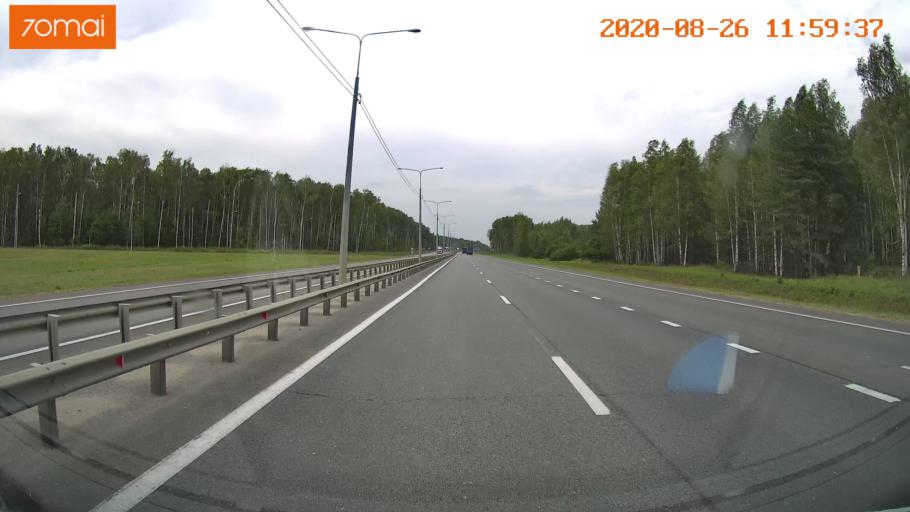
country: RU
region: Rjazan
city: Kiritsy
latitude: 54.2861
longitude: 40.2950
